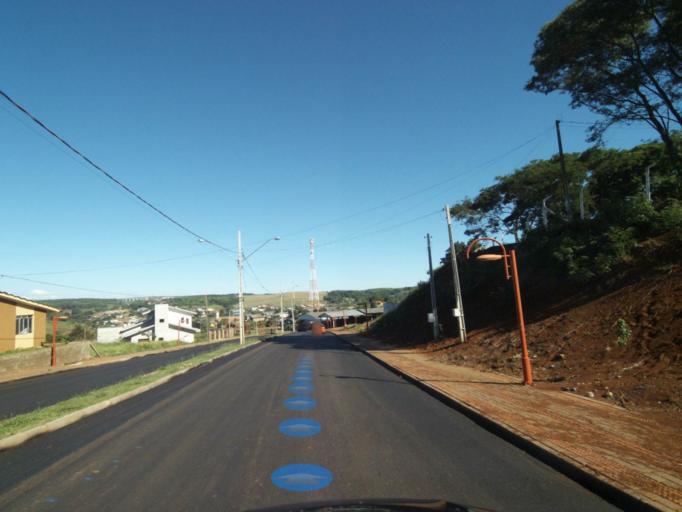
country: BR
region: Parana
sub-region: Coronel Vivida
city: Coronel Vivida
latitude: -26.1404
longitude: -52.3925
